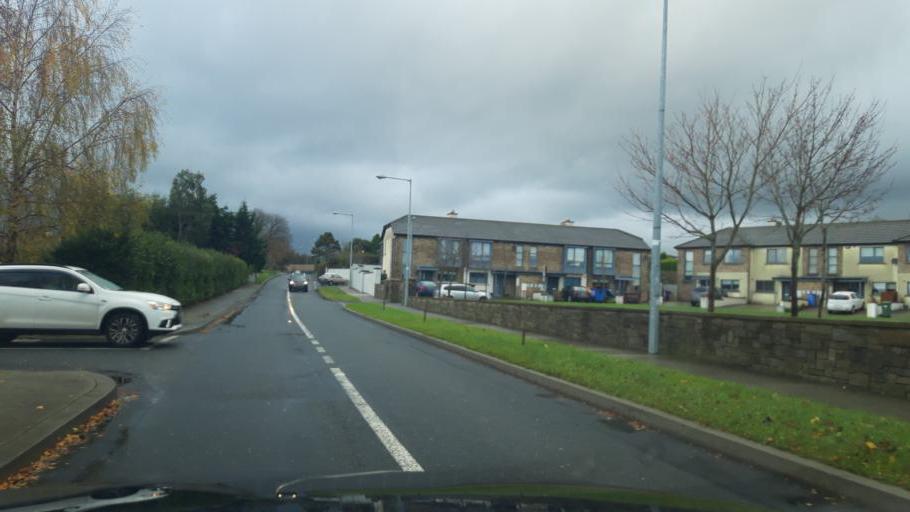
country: IE
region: Leinster
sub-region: Wicklow
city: Kilcoole
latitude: 53.1035
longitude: -6.0676
